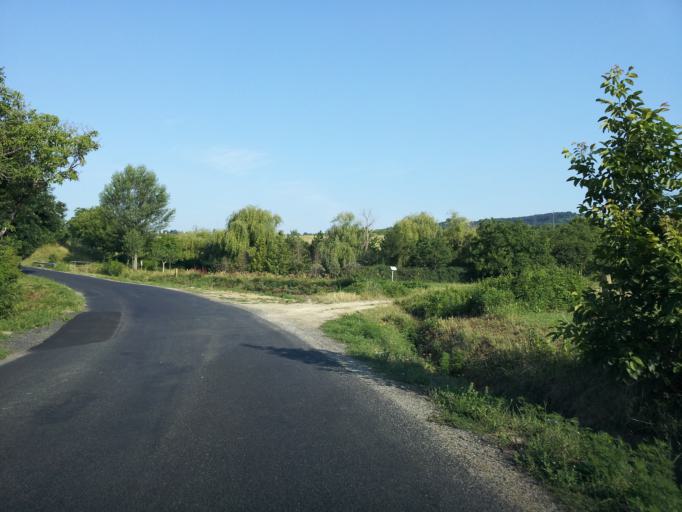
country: HU
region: Veszprem
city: Tapolca
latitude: 46.8484
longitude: 17.3491
